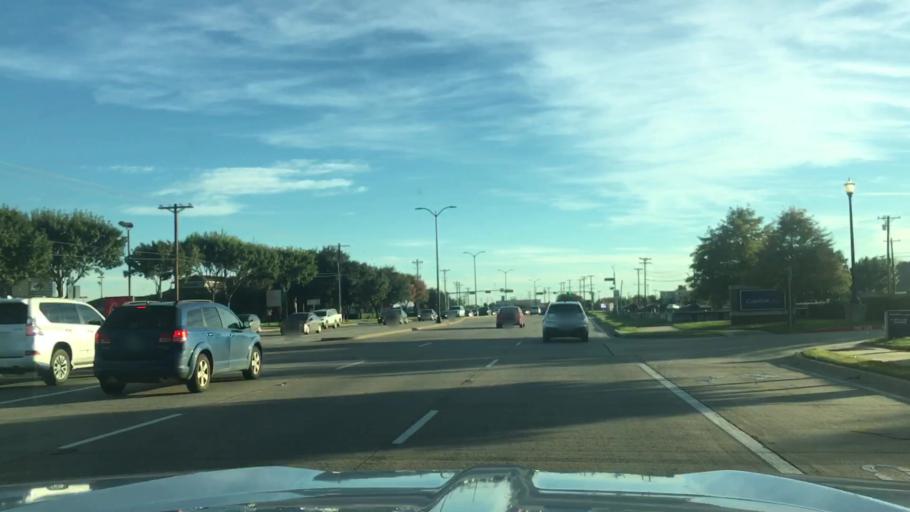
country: US
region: Texas
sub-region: Collin County
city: Frisco
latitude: 33.1516
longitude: -96.8038
